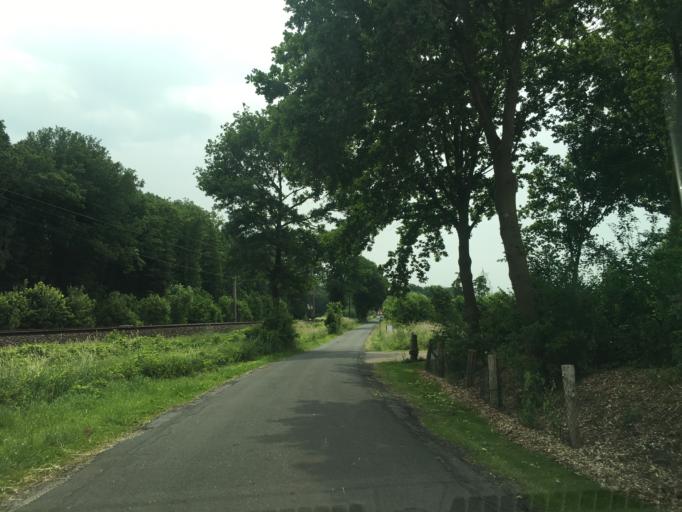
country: DE
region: North Rhine-Westphalia
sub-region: Regierungsbezirk Munster
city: Muenster
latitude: 52.0240
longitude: 7.6312
